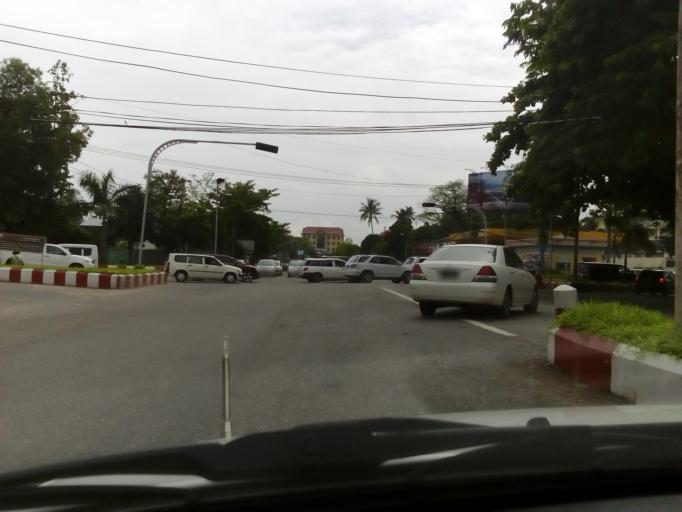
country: MM
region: Yangon
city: Yangon
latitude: 16.8667
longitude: 96.1326
